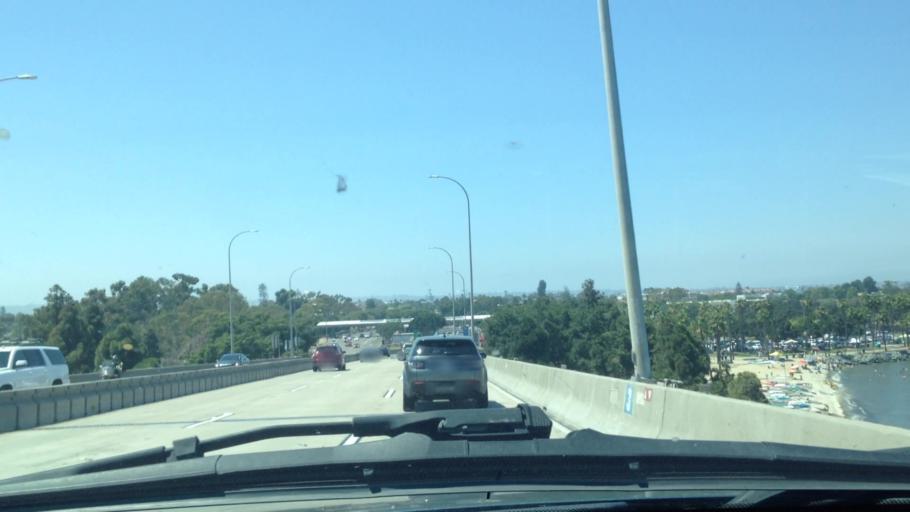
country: US
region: California
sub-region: San Diego County
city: Coronado
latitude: 32.6881
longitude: -117.1632
